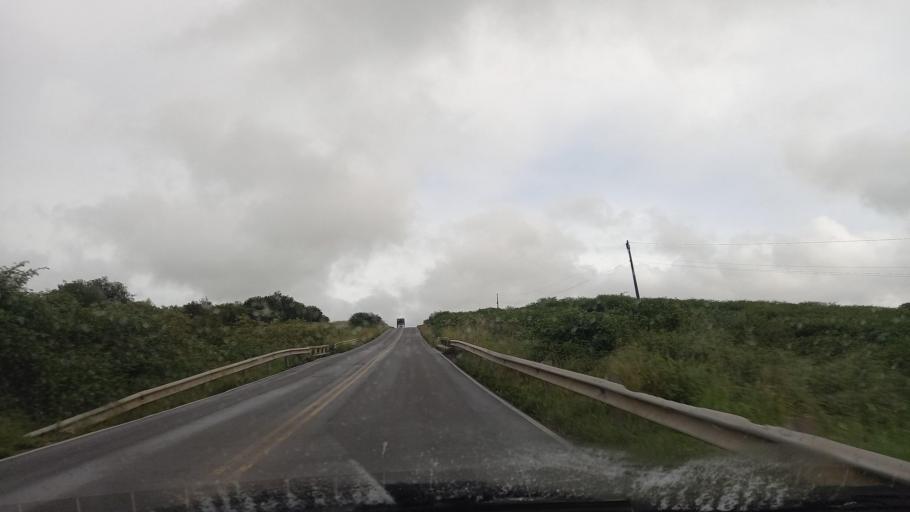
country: BR
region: Pernambuco
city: Garanhuns
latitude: -8.8459
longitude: -36.5247
